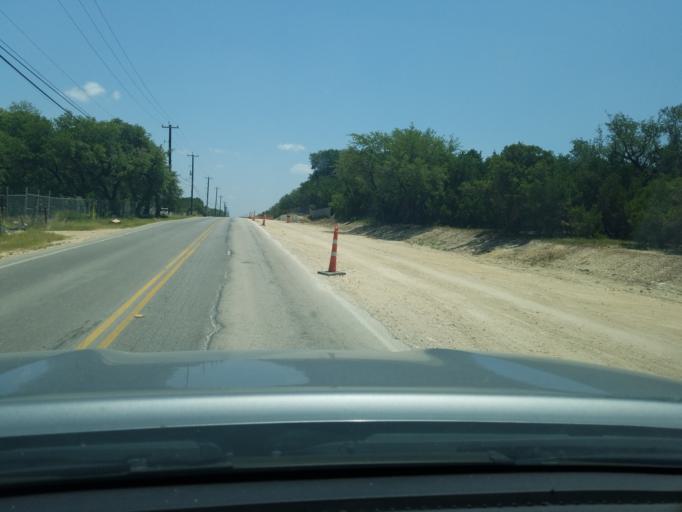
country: US
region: Texas
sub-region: Bexar County
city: Timberwood Park
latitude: 29.7084
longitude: -98.4972
